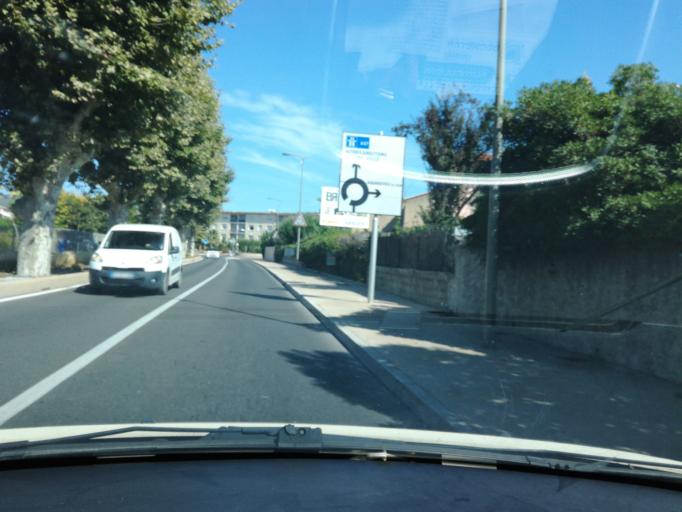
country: FR
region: Provence-Alpes-Cote d'Azur
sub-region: Departement du Var
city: La Crau
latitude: 43.1454
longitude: 6.0786
